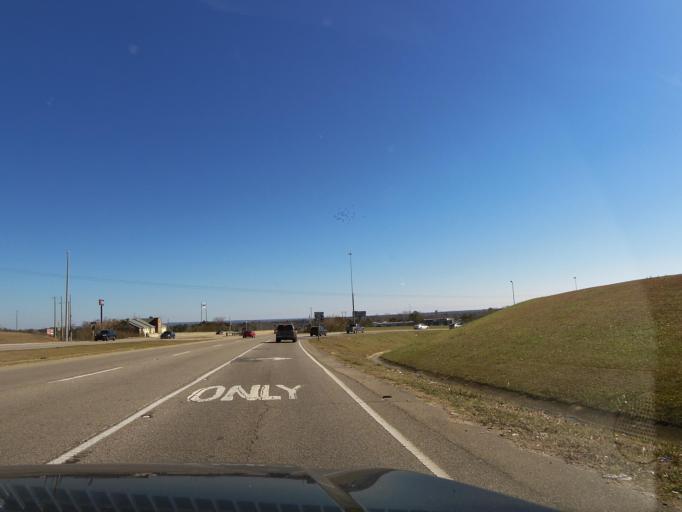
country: US
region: Alabama
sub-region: Elmore County
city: Millbrook
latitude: 32.4602
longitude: -86.3901
